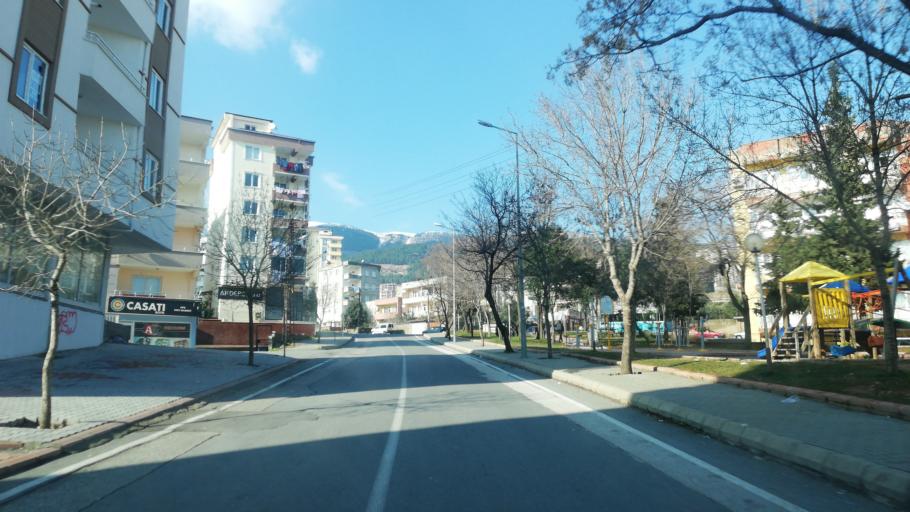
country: TR
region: Kahramanmaras
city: Kahramanmaras
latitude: 37.5904
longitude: 36.9056
